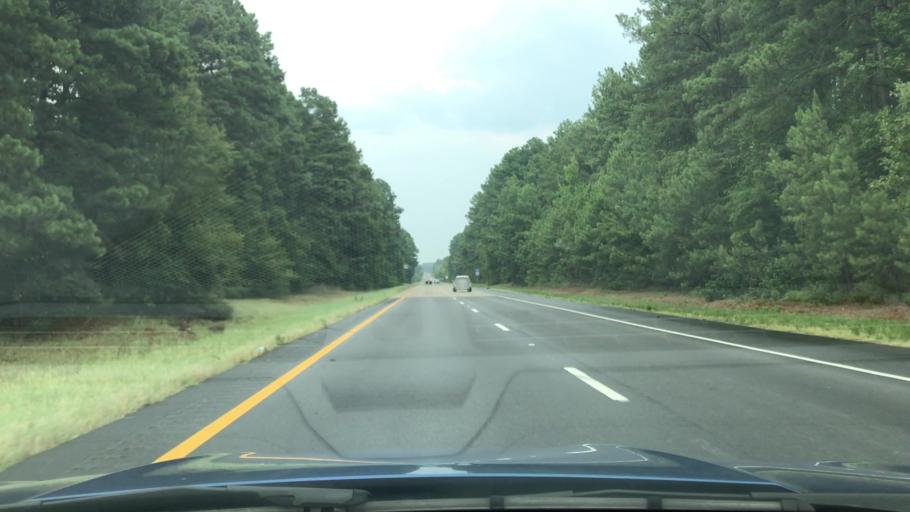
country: US
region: Texas
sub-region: Harrison County
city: Marshall
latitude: 32.4864
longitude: -94.4623
